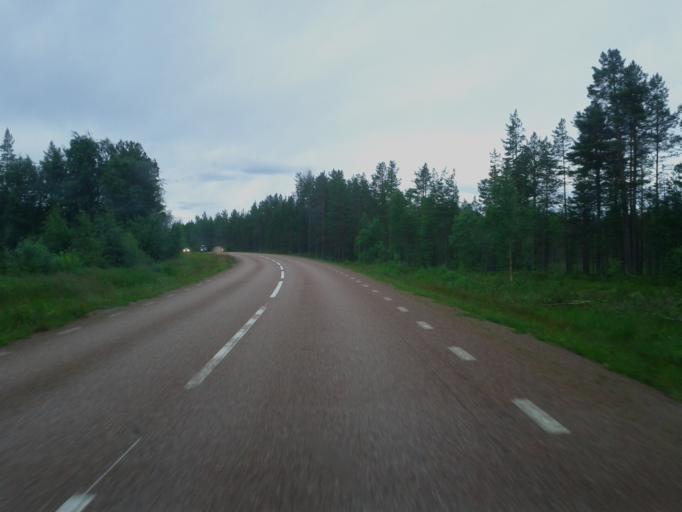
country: SE
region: Dalarna
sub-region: Alvdalens Kommun
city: AElvdalen
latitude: 61.5277
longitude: 13.3586
